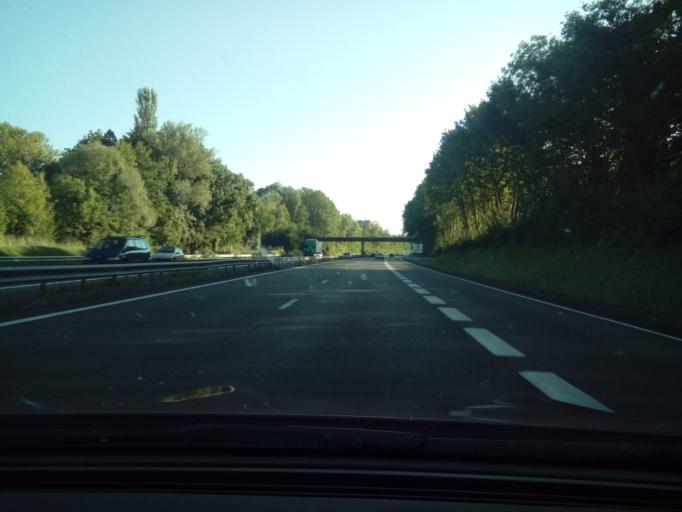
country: FR
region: Rhone-Alpes
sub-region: Departement de la Haute-Savoie
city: Saint-Felix
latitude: 45.8082
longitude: 5.9843
